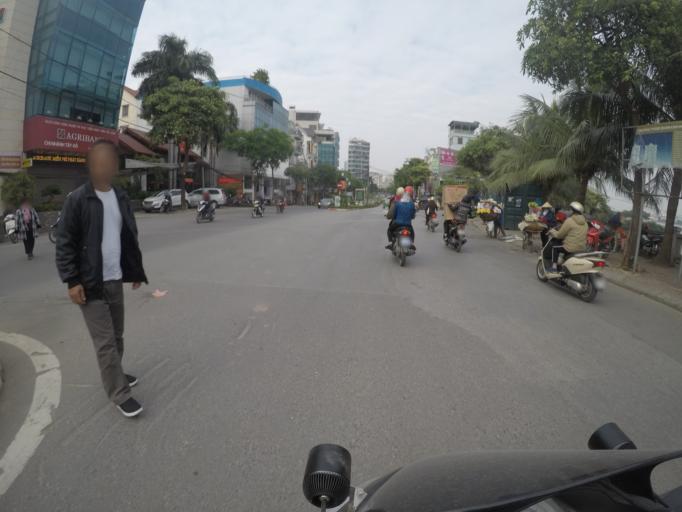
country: VN
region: Ha Noi
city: Tay Ho
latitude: 21.0595
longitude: 105.8089
